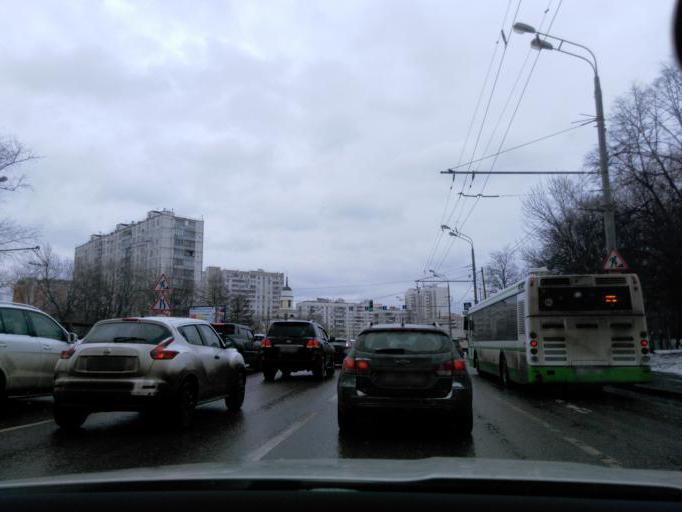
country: RU
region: Moscow
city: Likhobory
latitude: 55.8585
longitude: 37.5579
